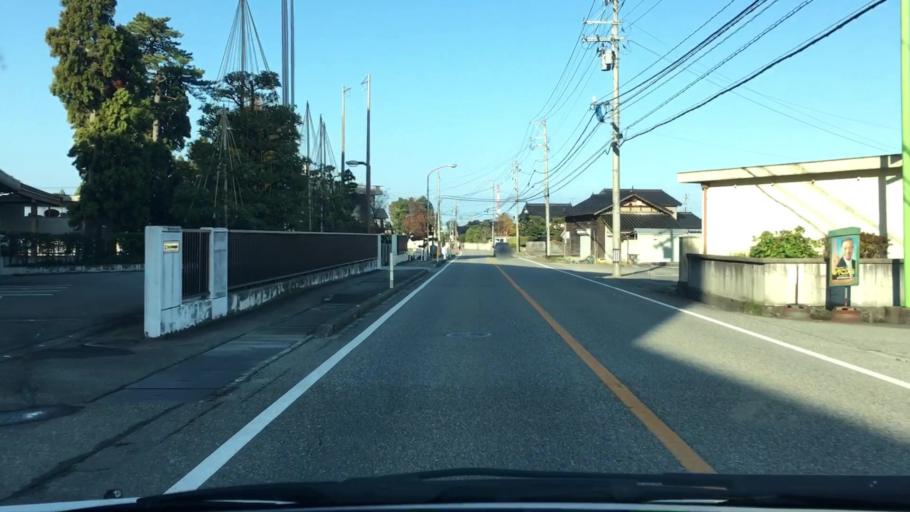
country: JP
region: Toyama
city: Kamiichi
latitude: 36.7045
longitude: 137.3128
